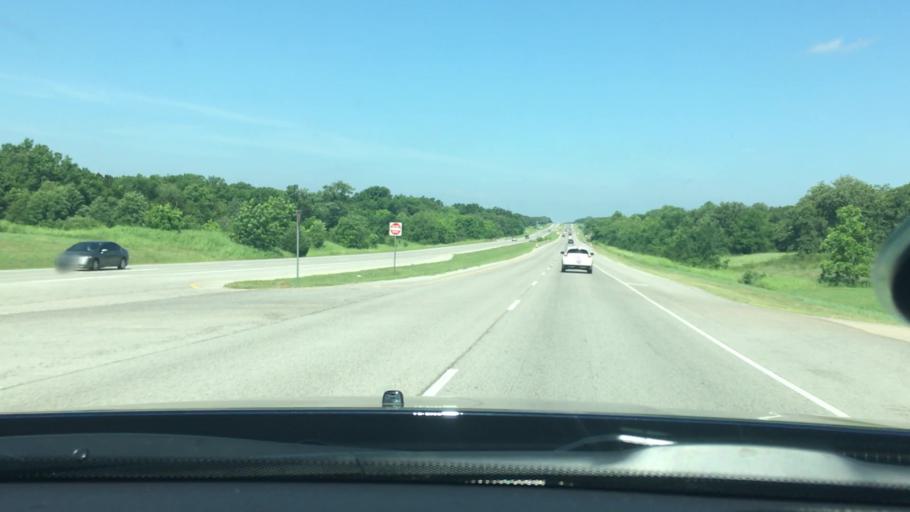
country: US
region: Oklahoma
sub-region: Carter County
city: Ardmore
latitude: 34.1342
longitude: -97.0989
